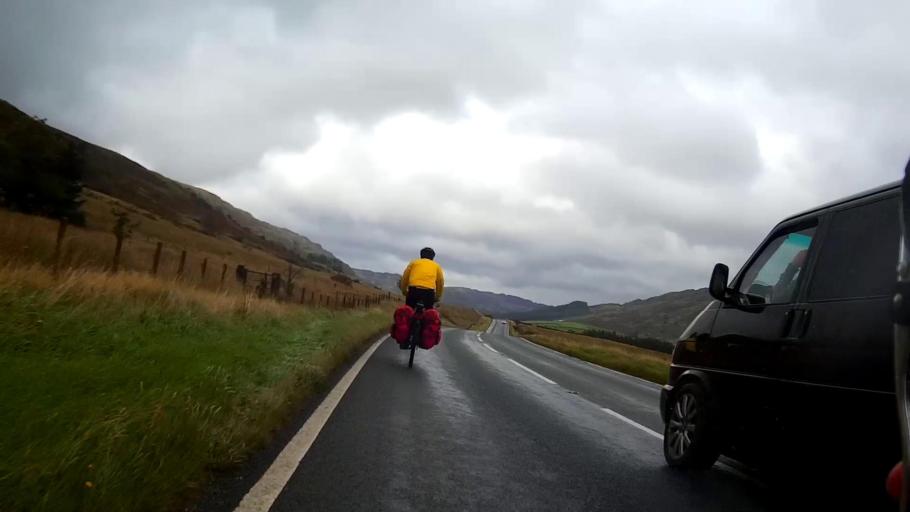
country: GB
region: Wales
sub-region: Gwynedd
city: Blaenau-Ffestiniog
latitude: 53.0911
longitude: -3.9631
